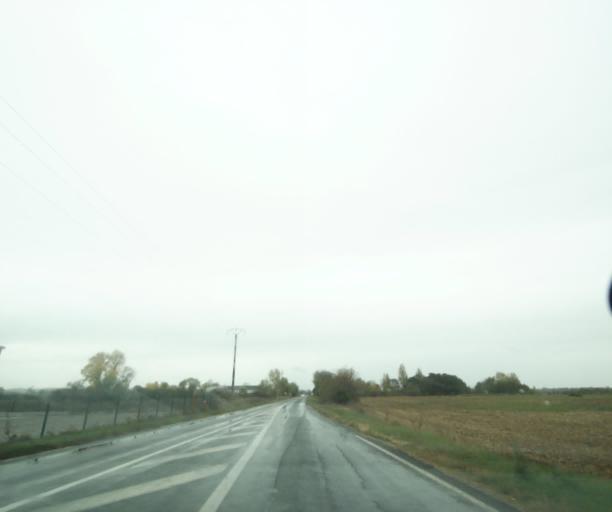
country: FR
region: Rhone-Alpes
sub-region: Departement de l'Ain
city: Loyettes
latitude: 45.7954
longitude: 5.2108
